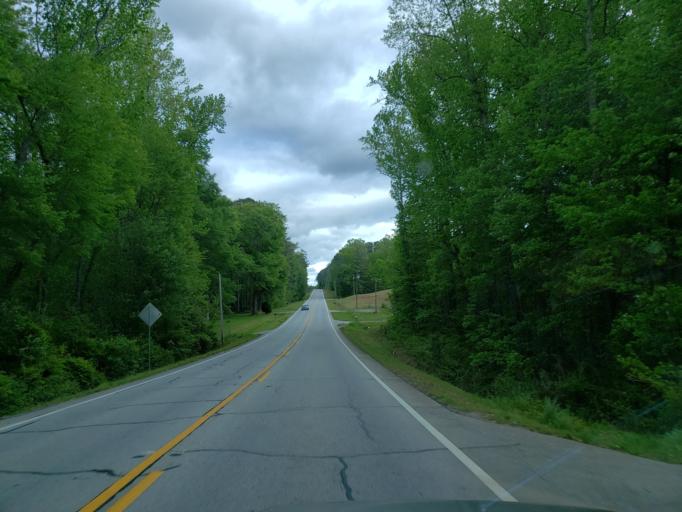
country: US
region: Georgia
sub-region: Haralson County
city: Buchanan
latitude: 33.8163
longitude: -85.1118
